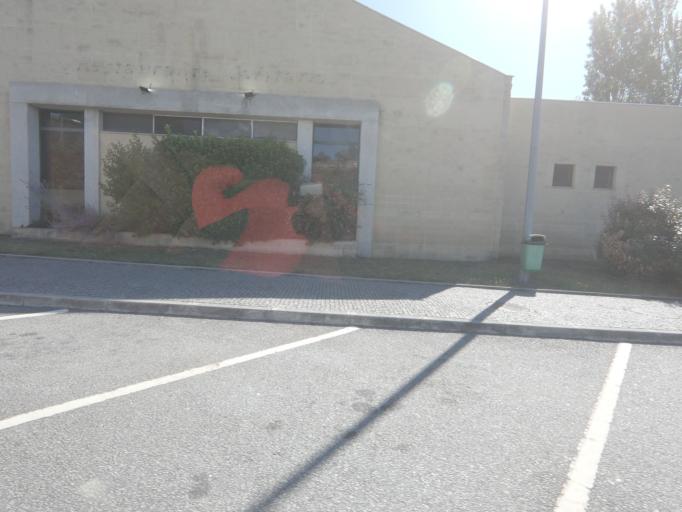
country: PT
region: Porto
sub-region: Marco de Canaveses
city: Marco de Canavezes
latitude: 41.2294
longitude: -8.1777
